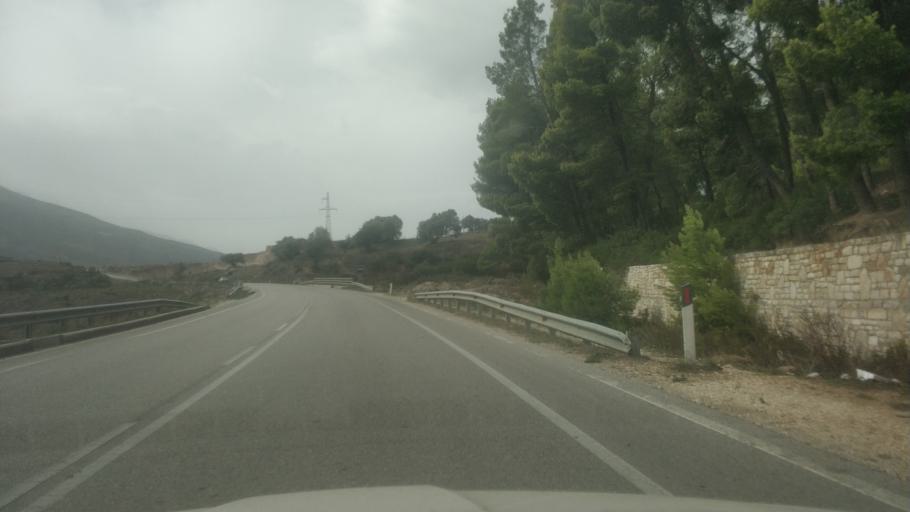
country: AL
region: Gjirokaster
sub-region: Rrethi i Tepelenes
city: Memaliaj
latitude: 40.3557
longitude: 19.9462
